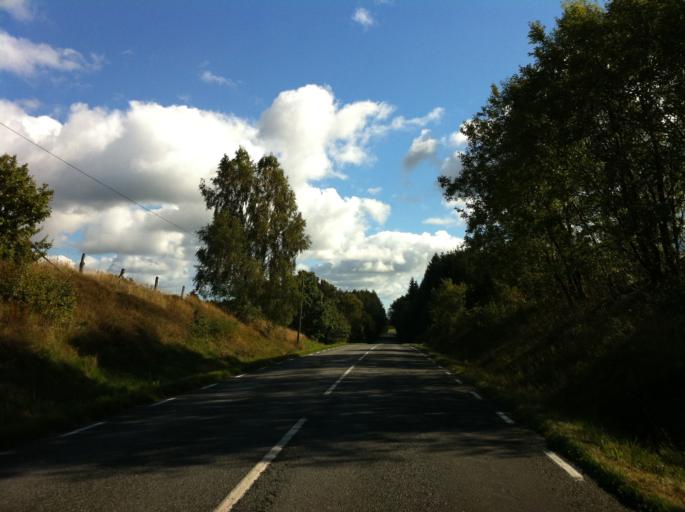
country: SE
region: Skane
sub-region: Kristianstads Kommun
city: Degeberga
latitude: 55.7715
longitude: 13.8993
